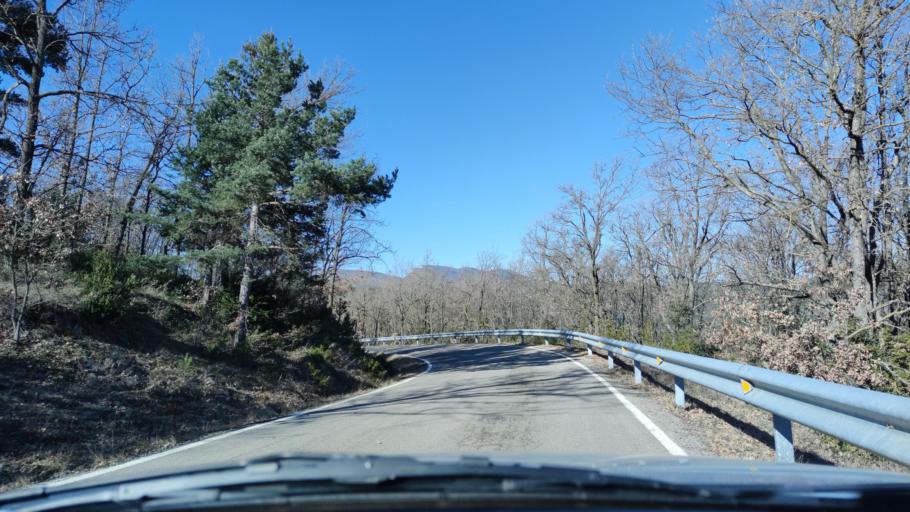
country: ES
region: Catalonia
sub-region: Provincia de Lleida
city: Artesa de Segre
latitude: 42.0477
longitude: 1.0744
